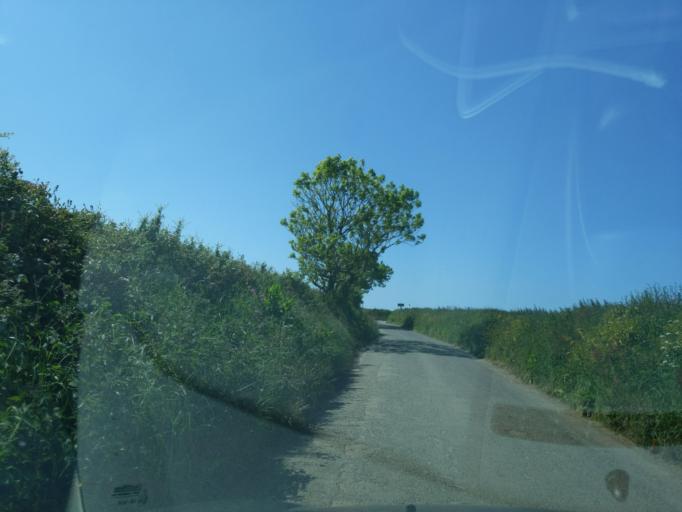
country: GB
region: England
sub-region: Cornwall
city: Wadebridge
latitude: 50.5807
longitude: -4.8342
